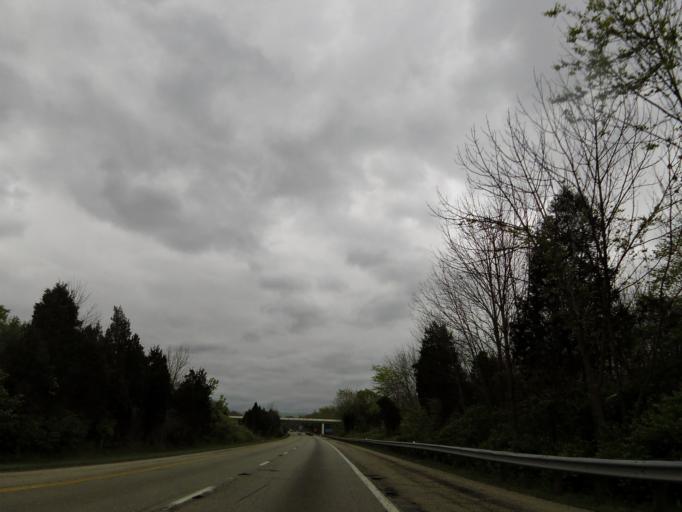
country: US
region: Ohio
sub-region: Warren County
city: Lebanon
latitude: 39.4013
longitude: -84.1804
